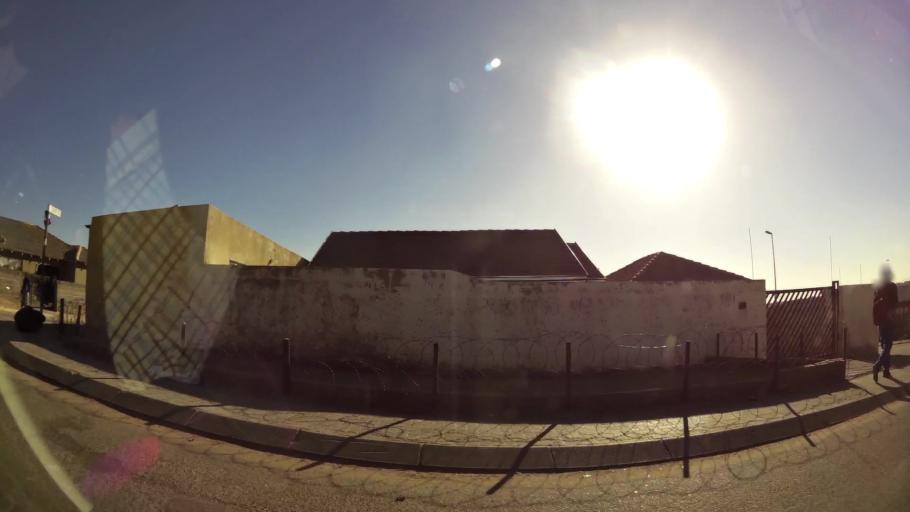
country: ZA
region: Gauteng
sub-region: Ekurhuleni Metropolitan Municipality
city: Tembisa
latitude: -26.0204
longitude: 28.2174
